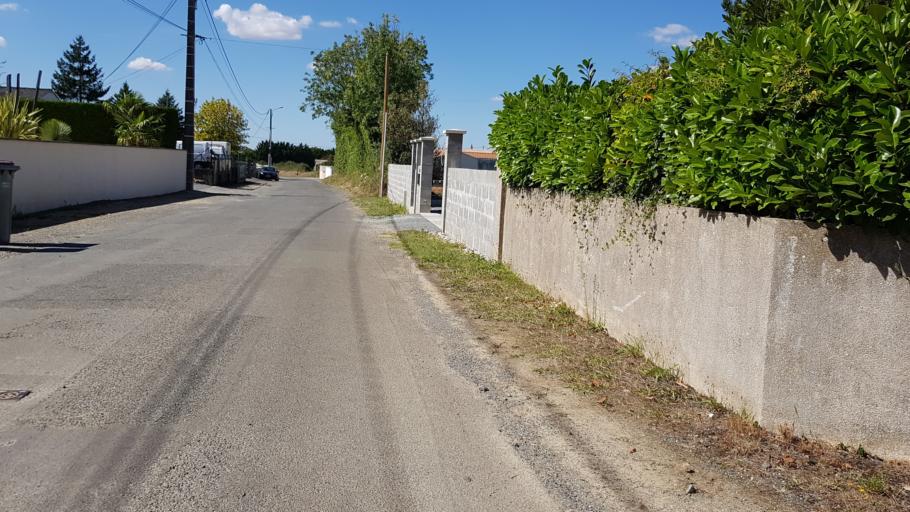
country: FR
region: Poitou-Charentes
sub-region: Departement des Deux-Sevres
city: Vouille
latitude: 46.3152
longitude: -0.3783
